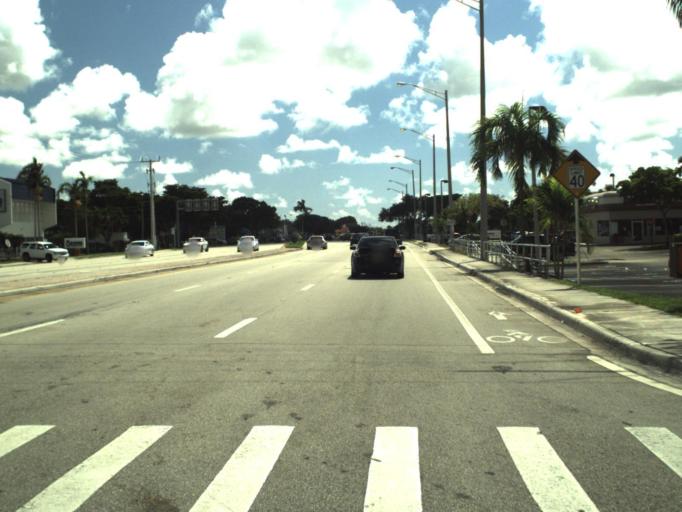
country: US
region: Florida
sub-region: Broward County
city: Pembroke Pines
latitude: 26.0090
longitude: -80.2479
